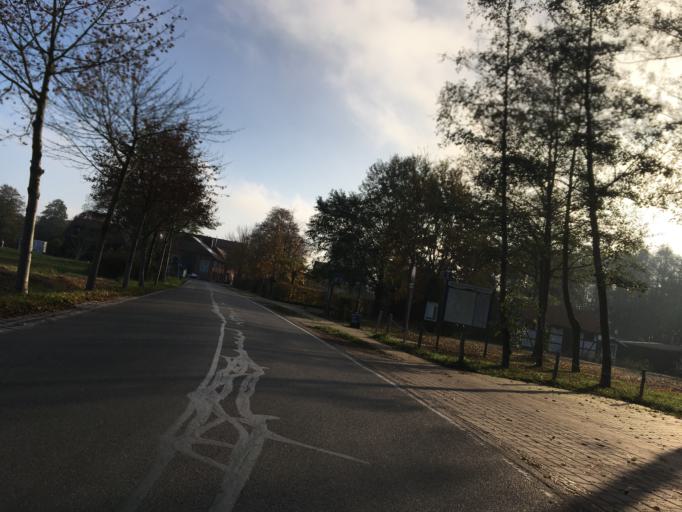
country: DE
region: Brandenburg
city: Schlepzig
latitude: 52.0290
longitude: 13.8864
